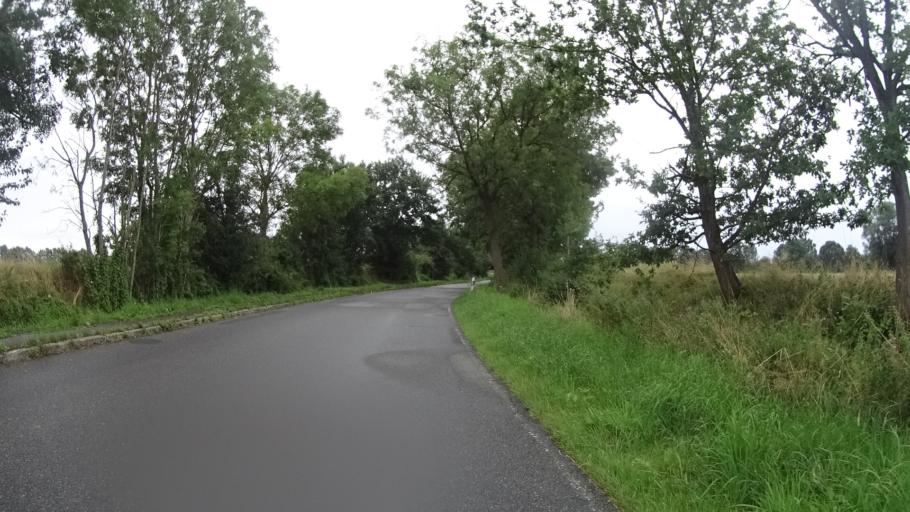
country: DE
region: Schleswig-Holstein
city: Lasbek
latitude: 53.7368
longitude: 10.3497
